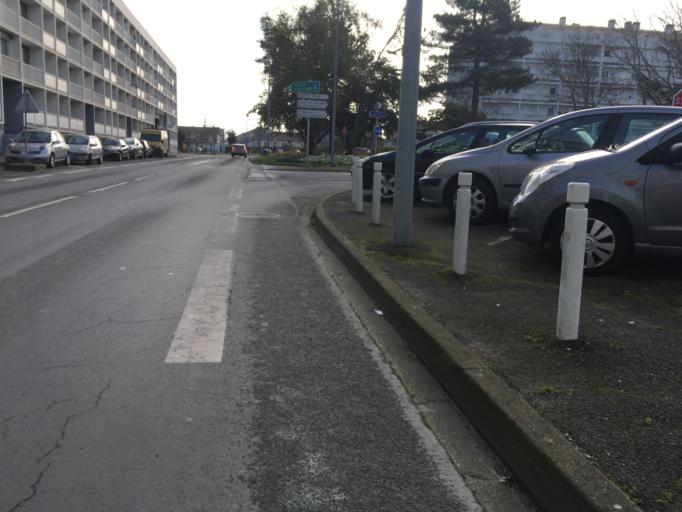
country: FR
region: Poitou-Charentes
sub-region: Departement de la Charente-Maritime
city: La Rochelle
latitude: 46.1674
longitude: -1.1794
